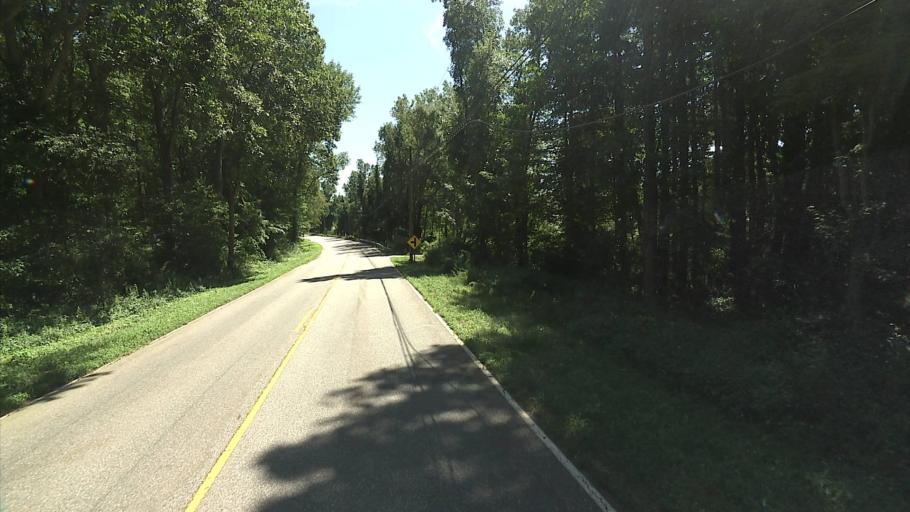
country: US
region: Connecticut
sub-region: New London County
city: Baltic
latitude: 41.6508
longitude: -72.0926
